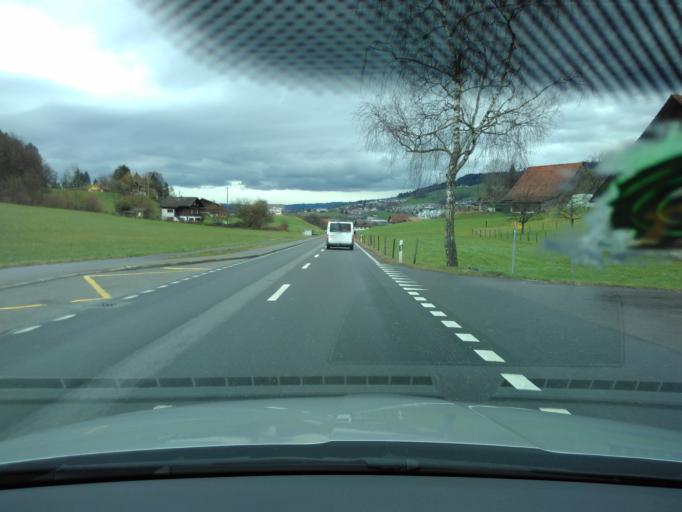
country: CH
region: Lucerne
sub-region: Lucerne-Land District
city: Root
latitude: 47.1229
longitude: 8.3730
